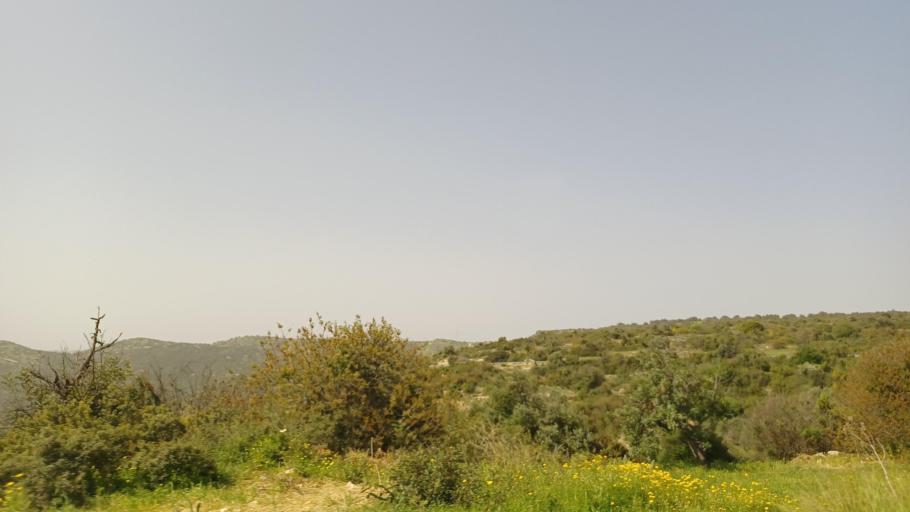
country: CY
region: Limassol
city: Pissouri
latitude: 34.7183
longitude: 32.7240
